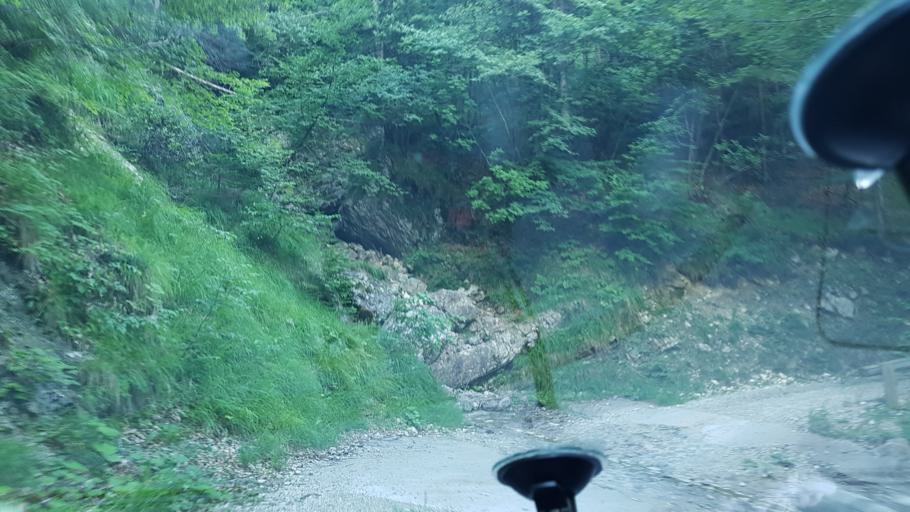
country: IT
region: Friuli Venezia Giulia
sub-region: Provincia di Udine
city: Dogna
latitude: 46.4400
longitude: 13.2987
